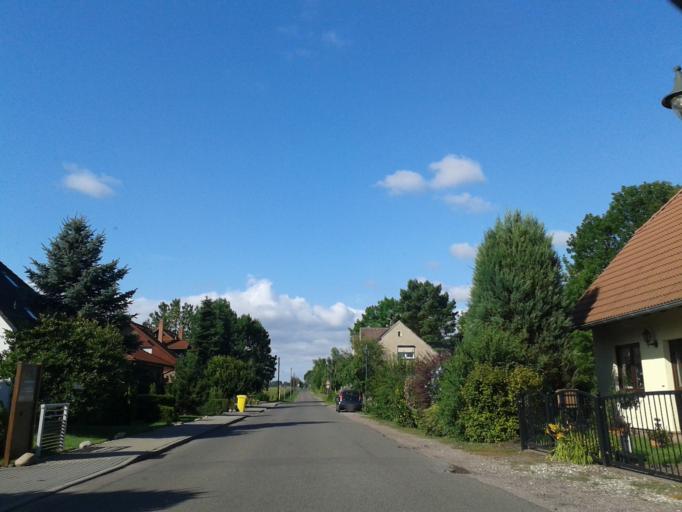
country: DE
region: Saxony-Anhalt
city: Braschwitz
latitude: 51.5205
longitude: 12.0552
